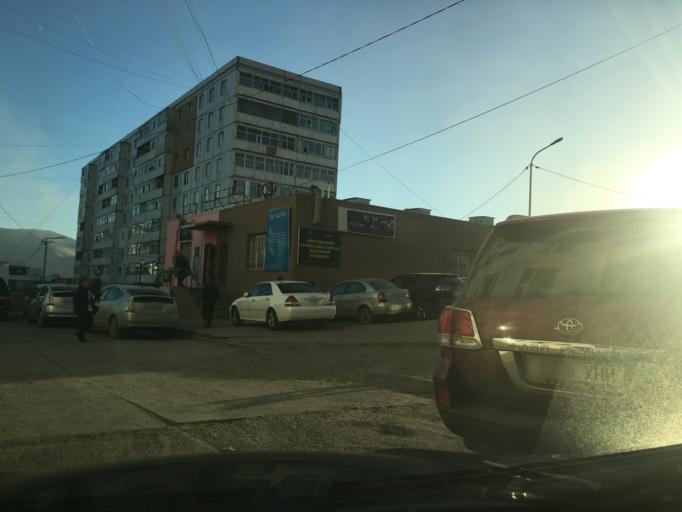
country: MN
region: Ulaanbaatar
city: Ulaanbaatar
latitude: 47.9247
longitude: 106.8819
